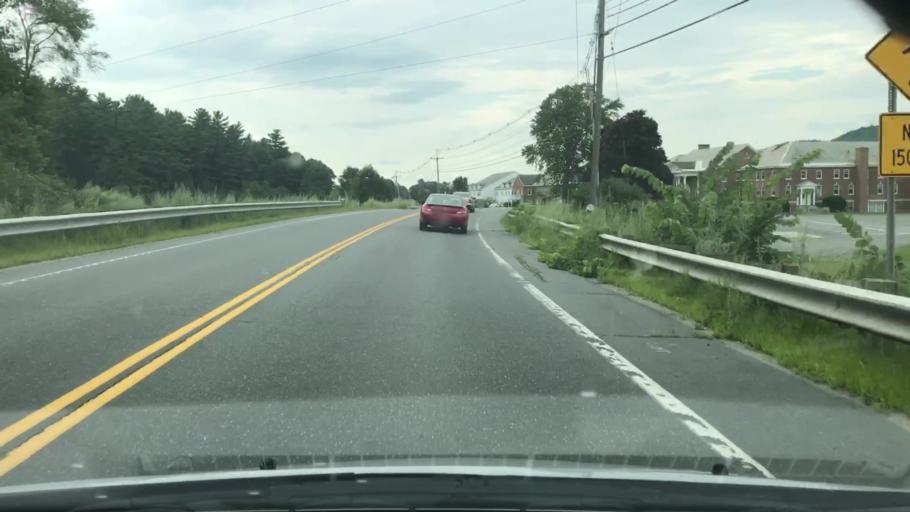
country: US
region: New Hampshire
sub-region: Grafton County
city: North Haverhill
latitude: 44.1174
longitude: -72.0392
